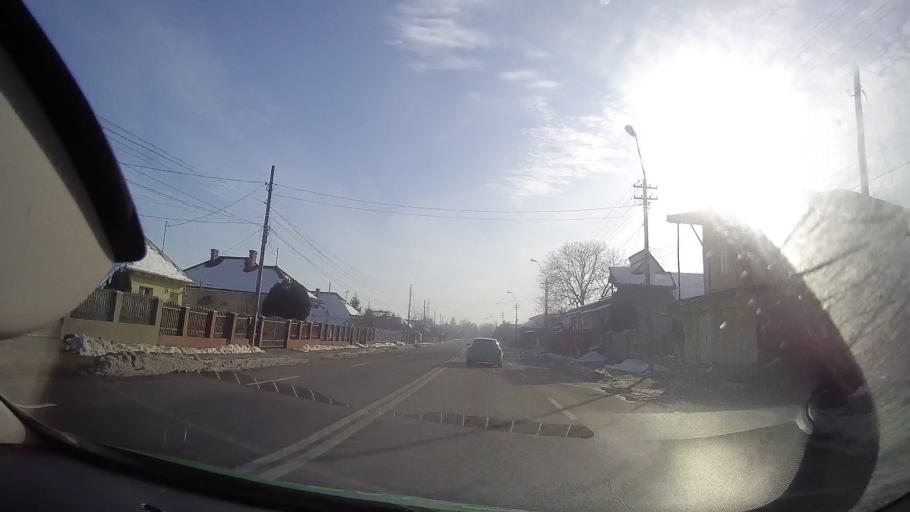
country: RO
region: Neamt
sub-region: Comuna Dobreni
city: Dobreni
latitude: 46.9523
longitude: 26.3839
